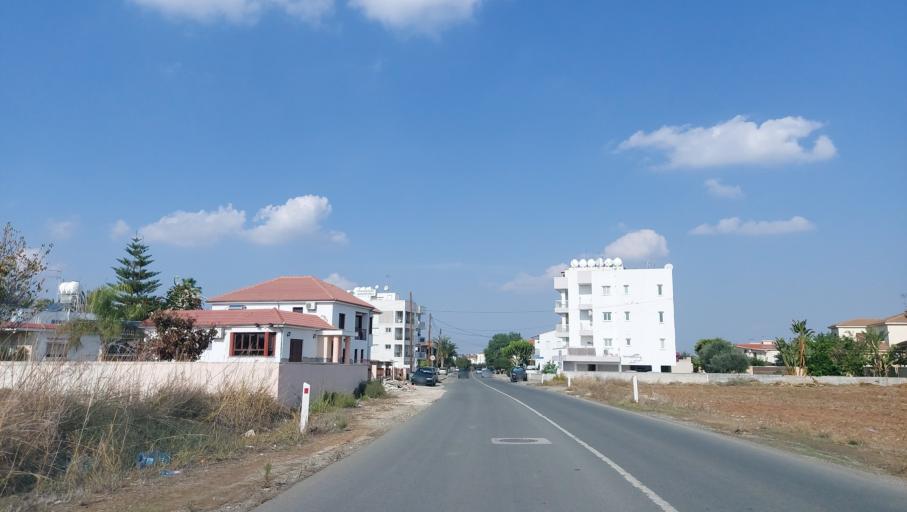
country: CY
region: Lefkosia
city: Tseri
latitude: 35.1021
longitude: 33.3072
